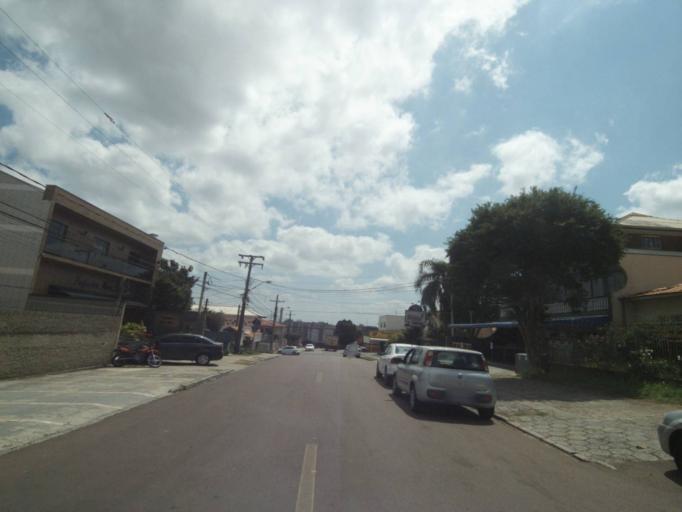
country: BR
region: Parana
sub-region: Curitiba
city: Curitiba
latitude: -25.5025
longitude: -49.3040
